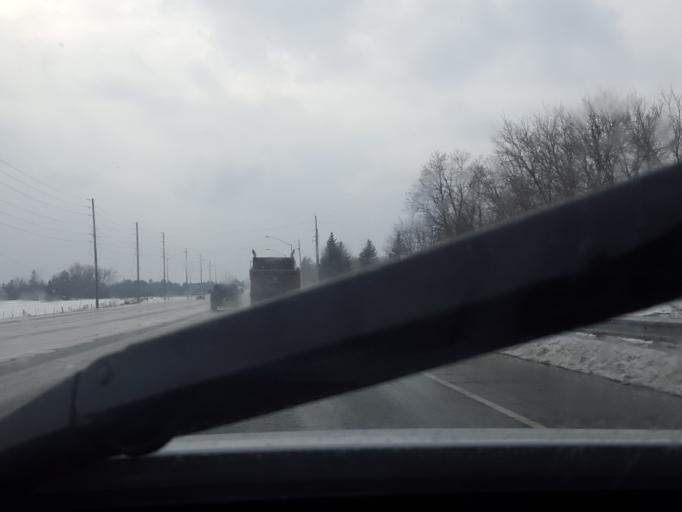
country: CA
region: Ontario
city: Newmarket
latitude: 43.9703
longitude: -79.4241
